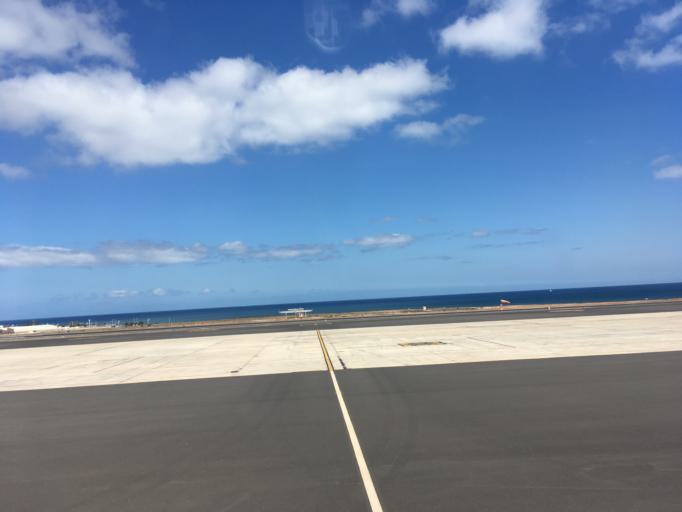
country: ES
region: Canary Islands
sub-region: Provincia de Las Palmas
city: Tias
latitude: 28.9503
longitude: -13.6063
